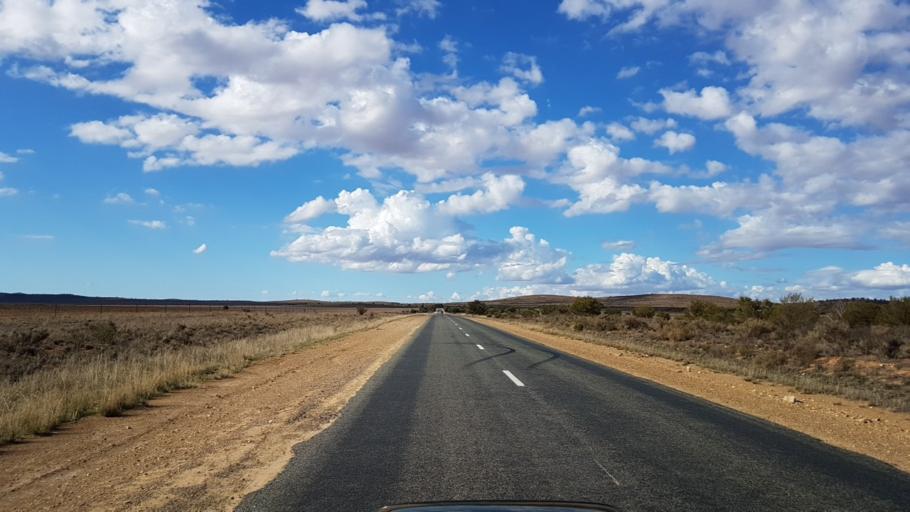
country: AU
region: South Australia
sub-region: Peterborough
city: Peterborough
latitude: -32.9658
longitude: 138.8764
